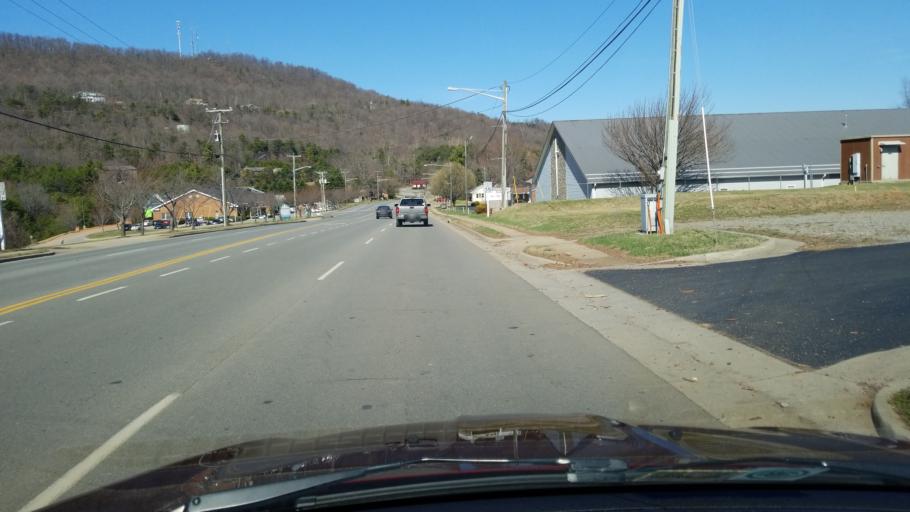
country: US
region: Virginia
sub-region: Franklin County
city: Rocky Mount
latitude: 37.0133
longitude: -79.8927
